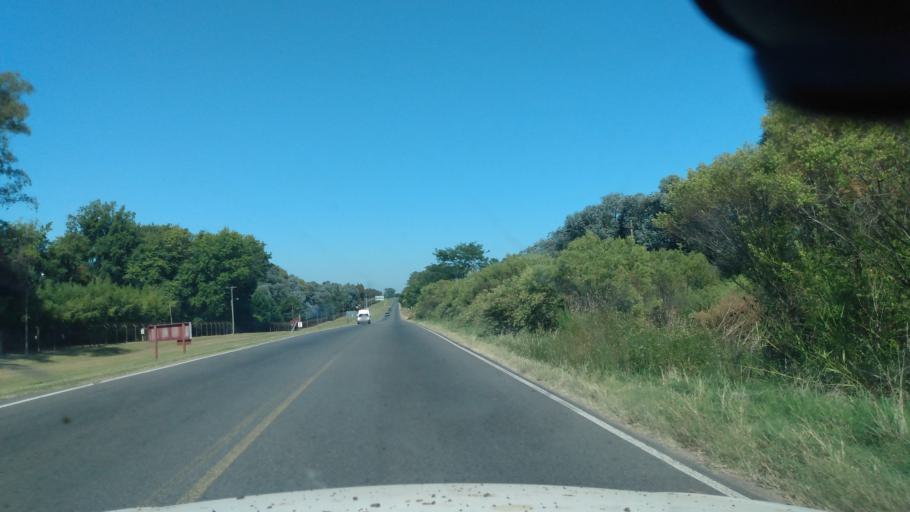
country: AR
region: Buenos Aires
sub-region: Partido de Lujan
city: Lujan
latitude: -34.5093
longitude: -59.0952
